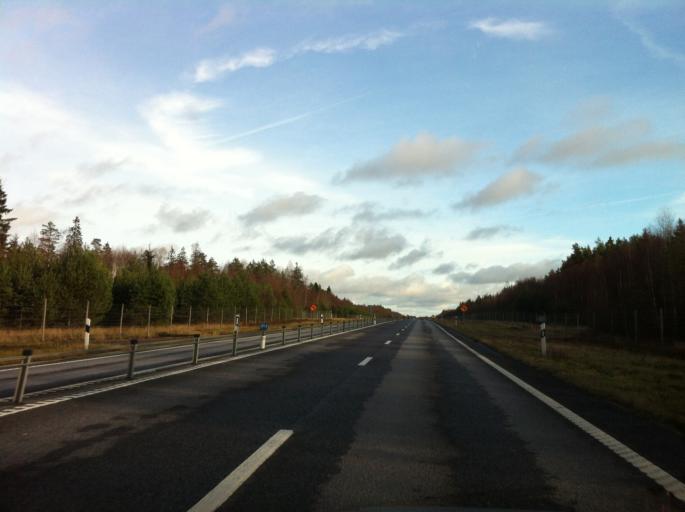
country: SE
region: Kronoberg
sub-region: Alvesta Kommun
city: Vislanda
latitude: 56.6657
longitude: 14.3047
